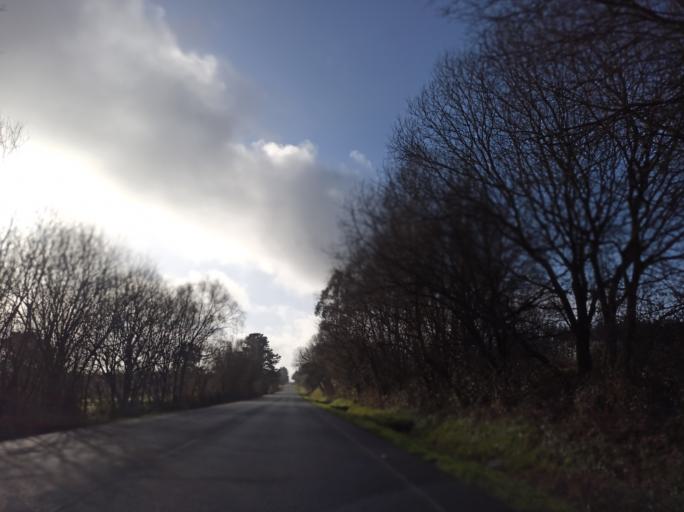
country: ES
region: Galicia
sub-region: Provincia da Coruna
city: Curtis
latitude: 43.0948
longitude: -8.0189
